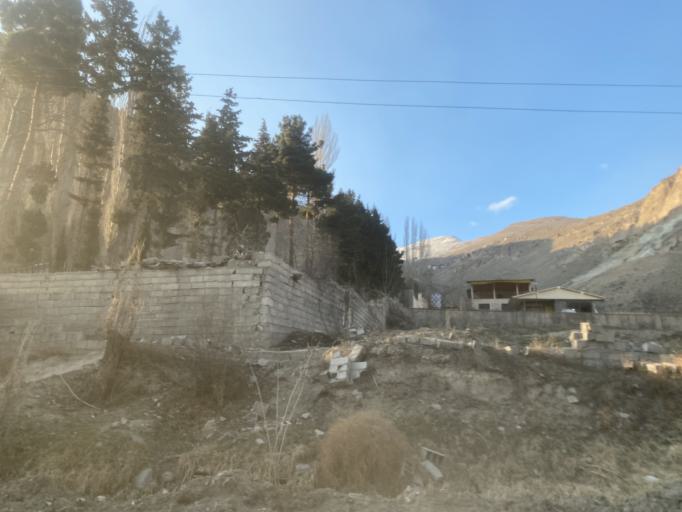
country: IR
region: Tehran
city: Damavand
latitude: 35.8924
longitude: 52.2070
